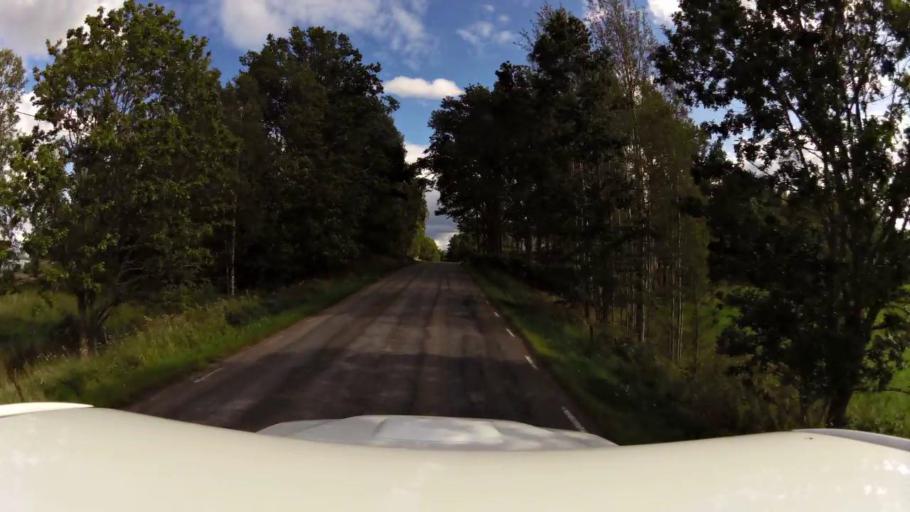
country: SE
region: OEstergoetland
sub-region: Kinda Kommun
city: Rimforsa
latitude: 58.2302
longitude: 15.6940
